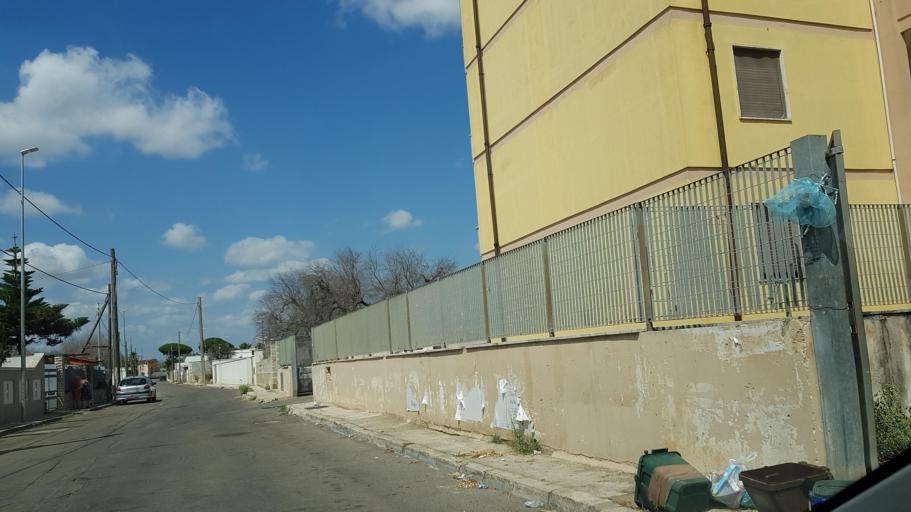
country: IT
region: Apulia
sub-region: Provincia di Lecce
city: Trepuzzi
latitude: 40.4078
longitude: 18.0623
